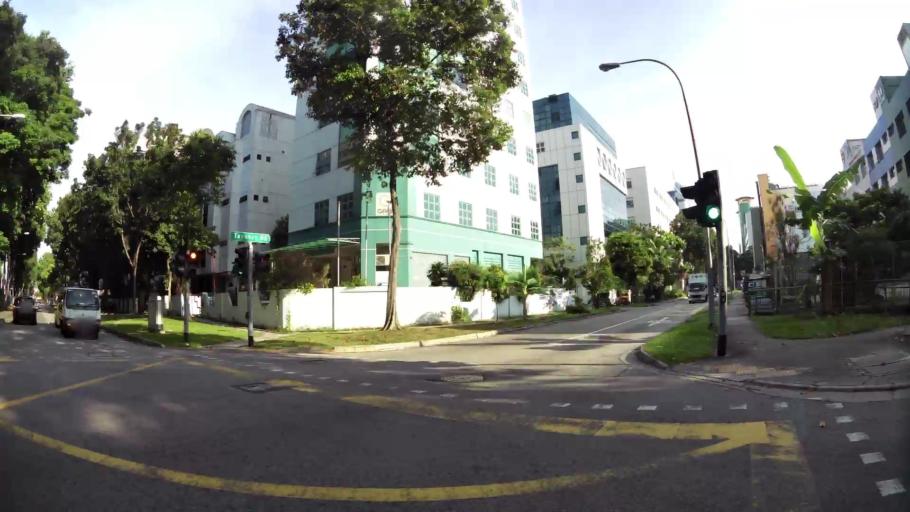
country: SG
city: Singapore
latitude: 1.3271
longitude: 103.8754
